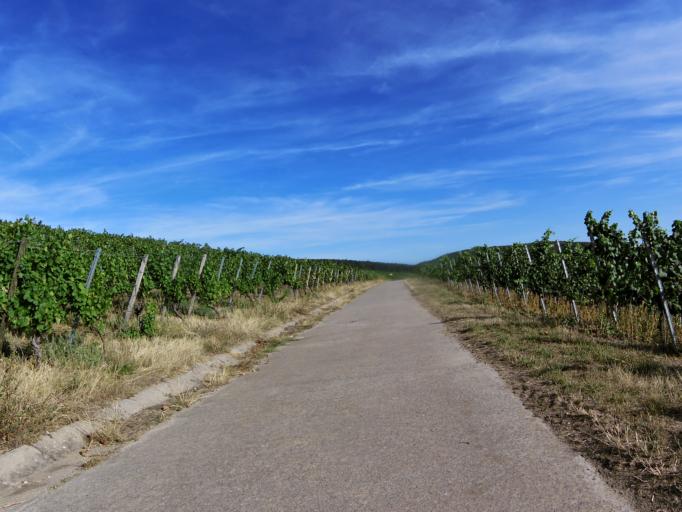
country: DE
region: Bavaria
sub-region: Regierungsbezirk Unterfranken
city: Randersacker
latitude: 49.7463
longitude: 9.9938
